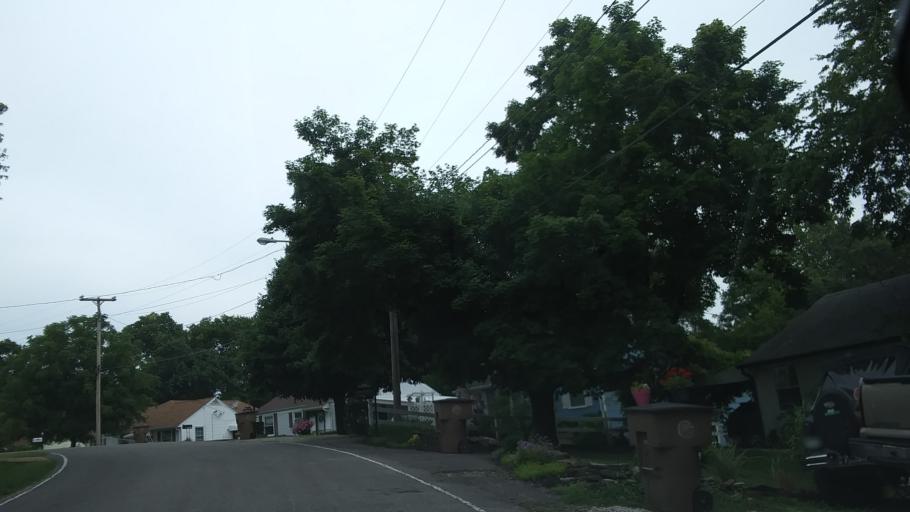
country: US
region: Tennessee
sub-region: Davidson County
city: Belle Meade
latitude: 36.1417
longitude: -86.8524
